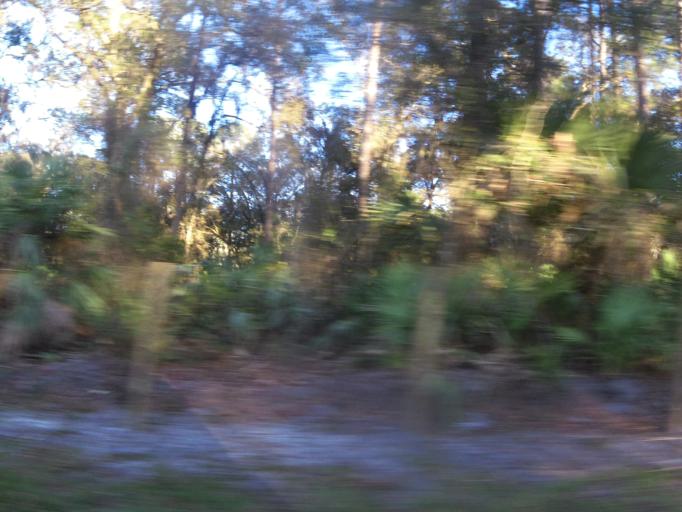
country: US
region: Florida
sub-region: Saint Johns County
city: Saint Augustine Shores
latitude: 29.7858
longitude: -81.4588
